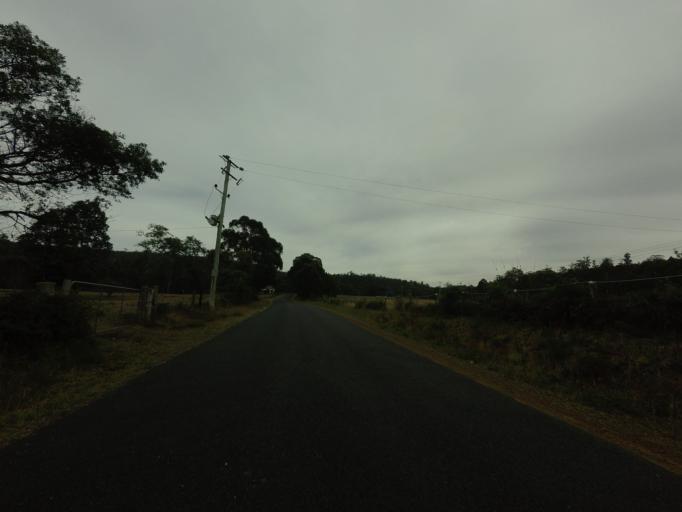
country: AU
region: Tasmania
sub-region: Sorell
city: Sorell
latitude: -42.5601
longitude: 147.5690
